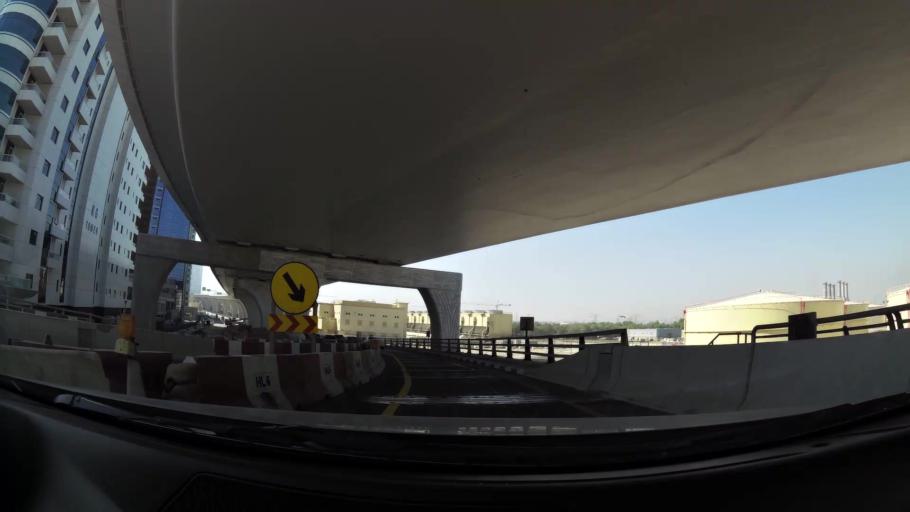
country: AE
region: Dubai
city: Dubai
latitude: 25.0696
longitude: 55.1267
